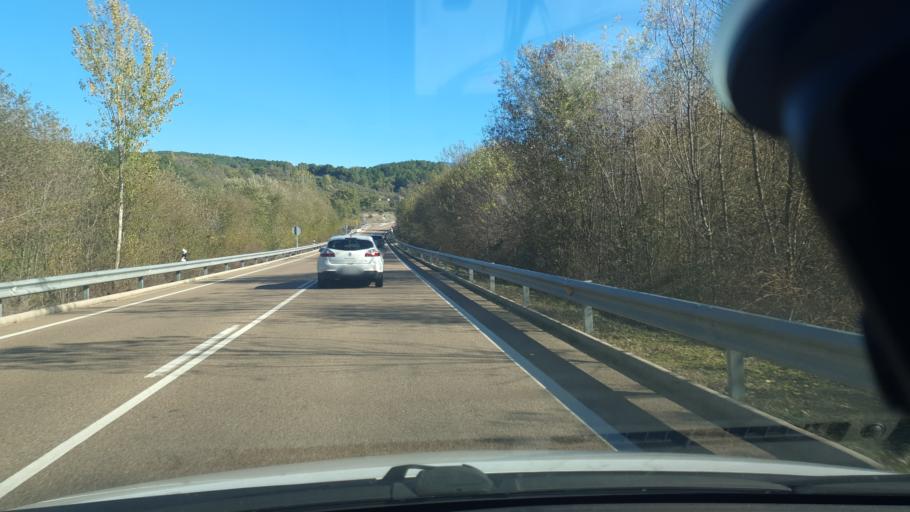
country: ES
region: Castille and Leon
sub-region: Provincia de Avila
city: Arenas de San Pedro
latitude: 40.1876
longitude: -5.0791
